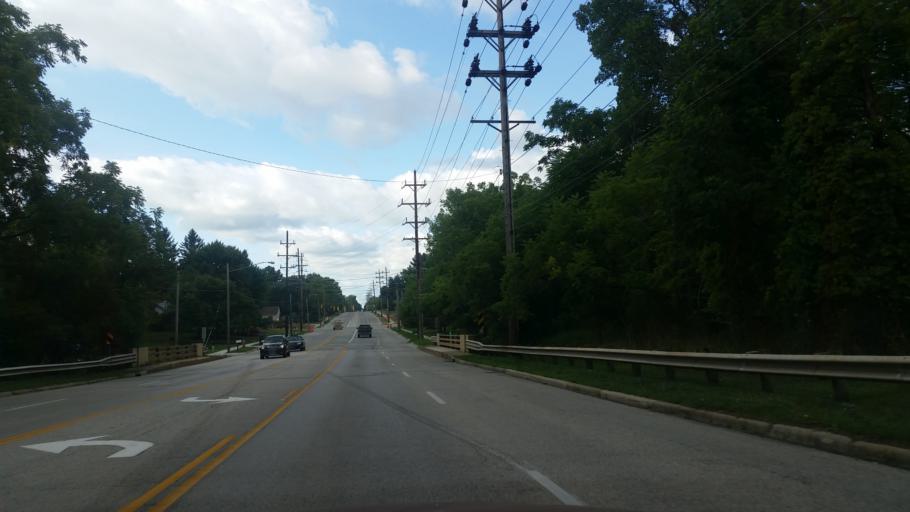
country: US
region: Ohio
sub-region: Cuyahoga County
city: Middleburg Heights
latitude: 41.3657
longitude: -81.7850
